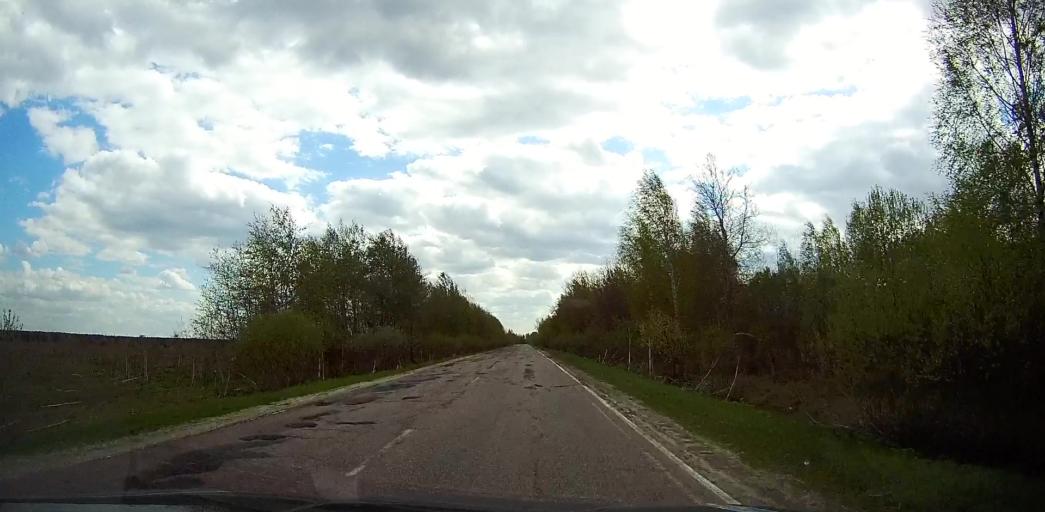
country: RU
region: Moskovskaya
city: Davydovo
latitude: 55.6378
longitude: 38.7477
